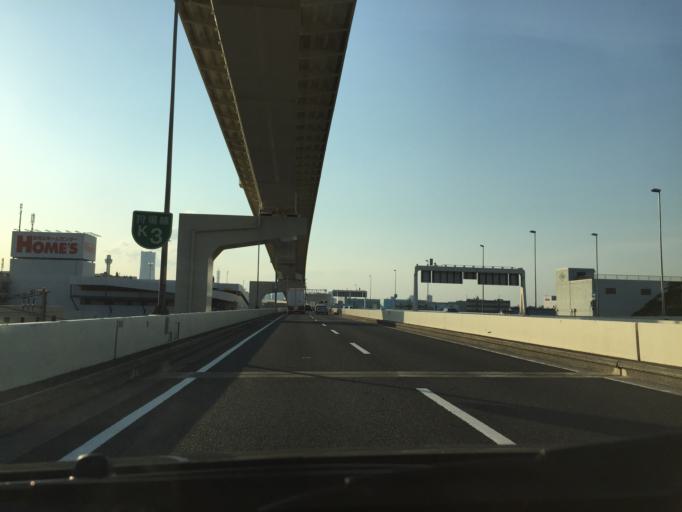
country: JP
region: Kanagawa
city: Yokohama
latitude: 35.4387
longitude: 139.6625
